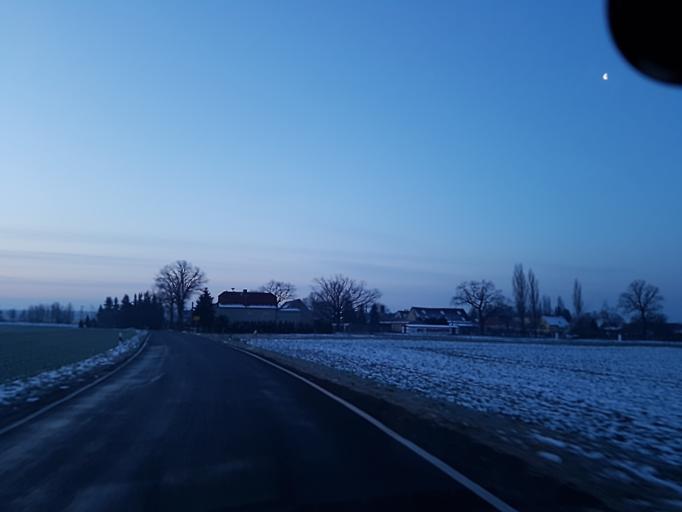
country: DE
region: Saxony
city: Oschatz
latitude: 51.3321
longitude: 13.1295
